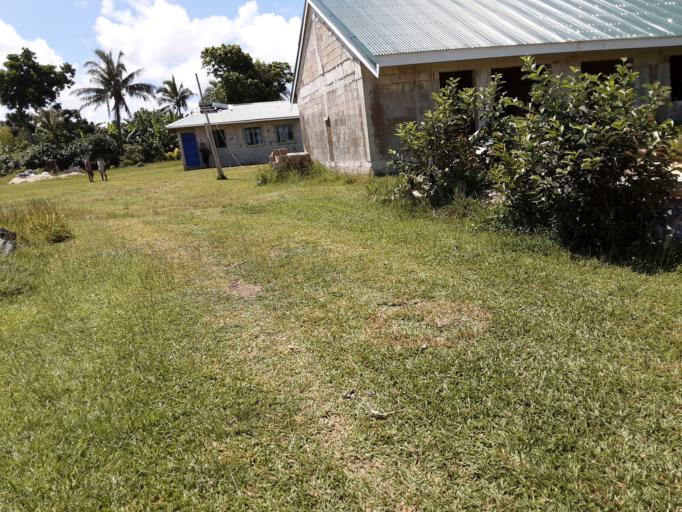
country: VU
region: Sanma
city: Luganville
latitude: -15.5210
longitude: 167.2527
